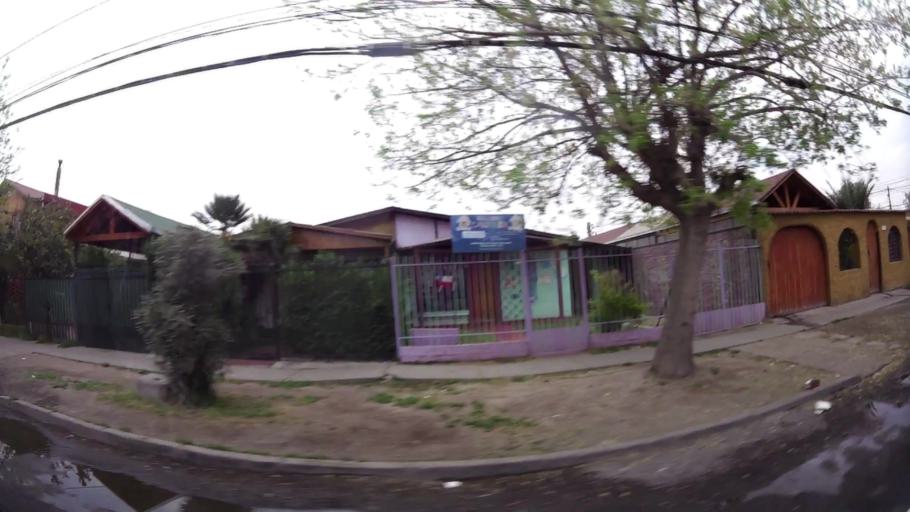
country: CL
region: Santiago Metropolitan
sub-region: Provincia de Santiago
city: Lo Prado
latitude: -33.4914
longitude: -70.7356
